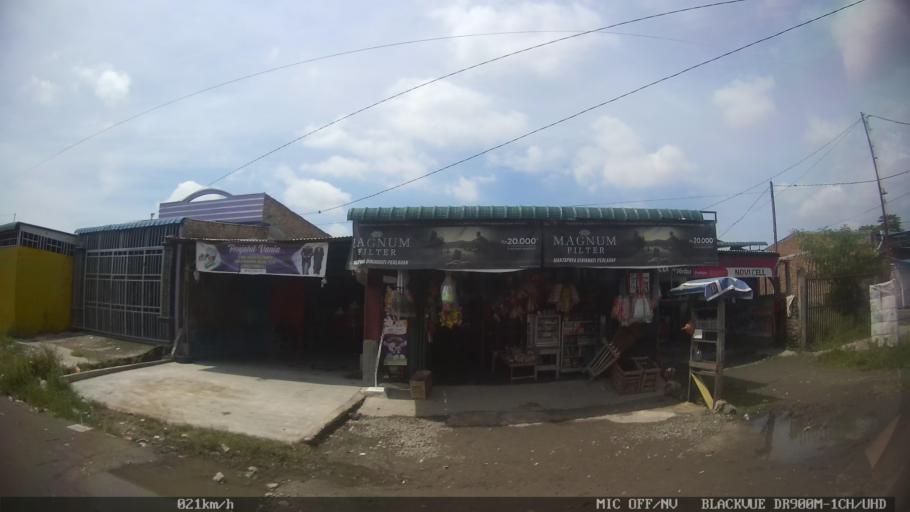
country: ID
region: North Sumatra
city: Medan
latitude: 3.6507
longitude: 98.7083
